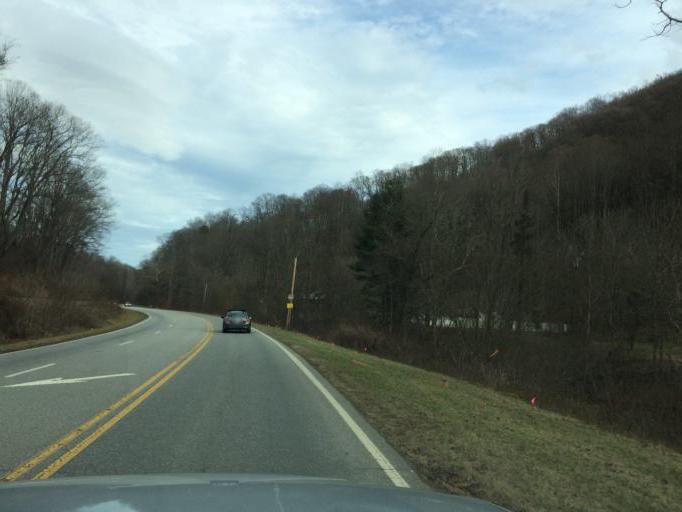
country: US
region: North Carolina
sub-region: Haywood County
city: Canton
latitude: 35.5377
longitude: -82.7801
